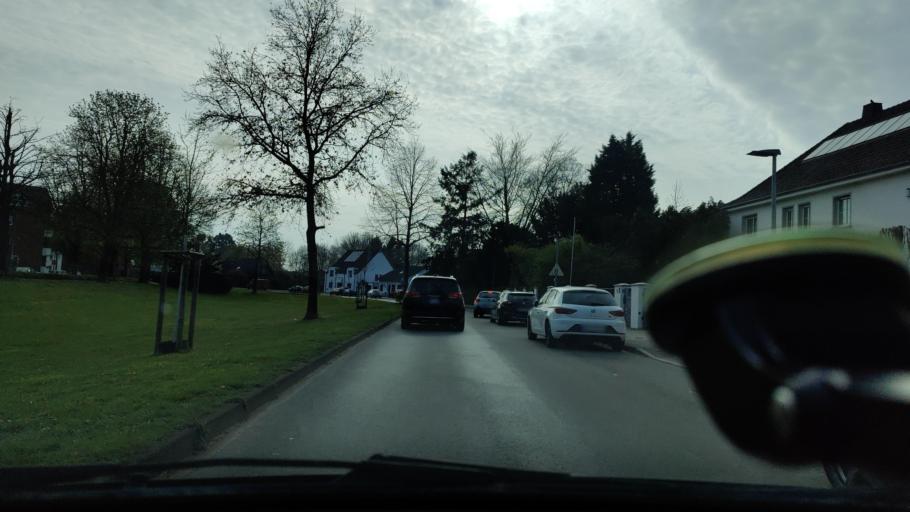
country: DE
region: North Rhine-Westphalia
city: Rheinberg
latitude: 51.5473
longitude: 6.5984
